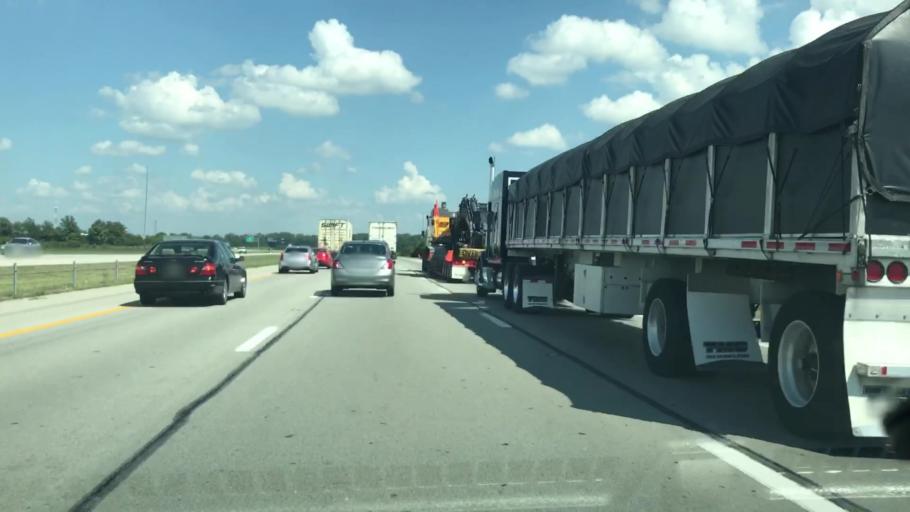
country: US
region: Ohio
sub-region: Clark County
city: Springfield
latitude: 39.8898
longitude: -83.7413
